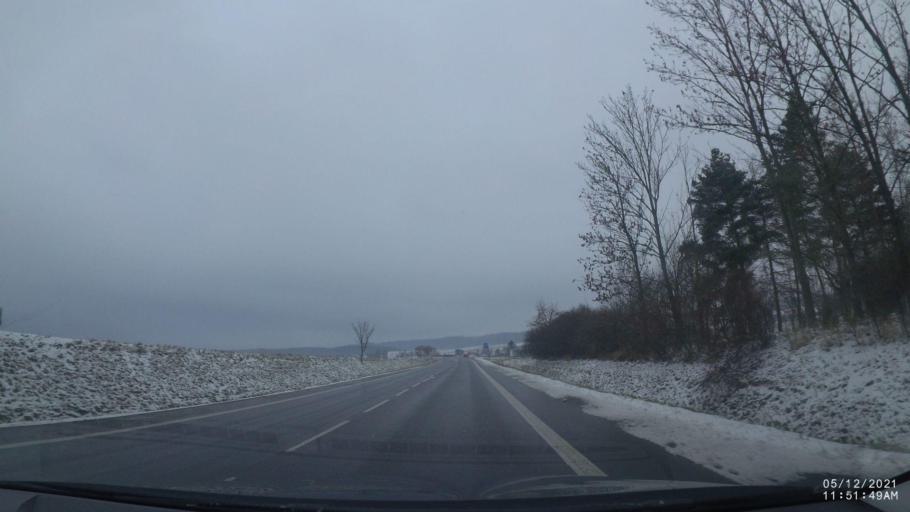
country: CZ
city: Dobruska
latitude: 50.2913
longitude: 16.1695
